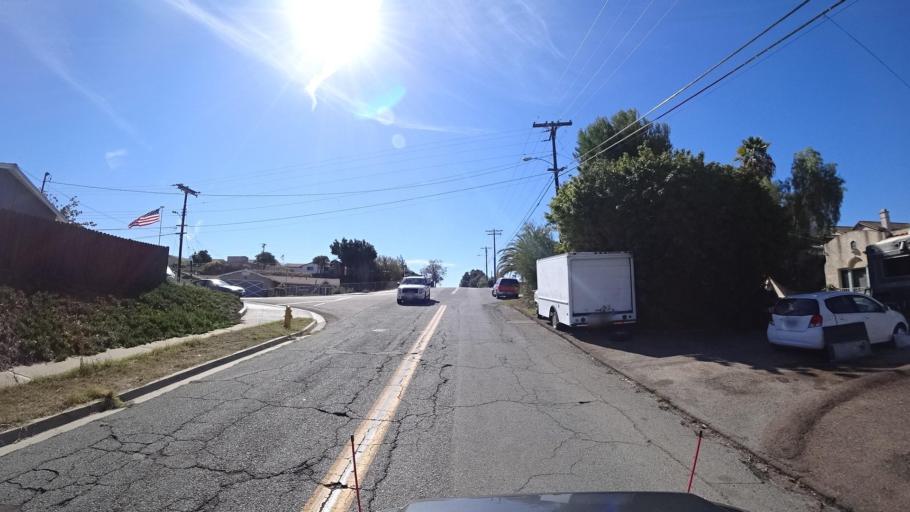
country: US
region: California
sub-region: San Diego County
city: Lemon Grove
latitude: 32.7209
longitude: -117.0231
